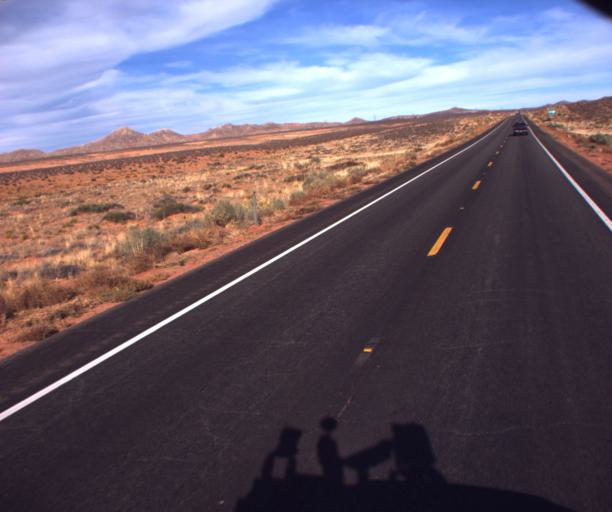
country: US
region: Arizona
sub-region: Apache County
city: Many Farms
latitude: 36.9270
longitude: -109.5842
